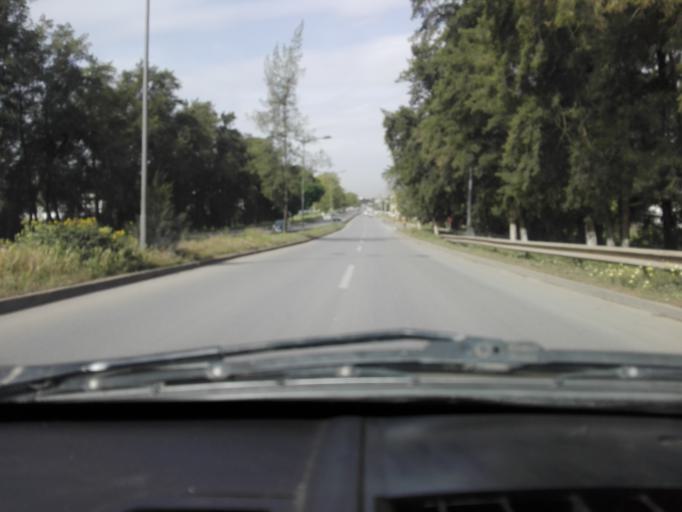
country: DZ
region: Alger
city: Dar el Beida
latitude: 36.7272
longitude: 3.2094
